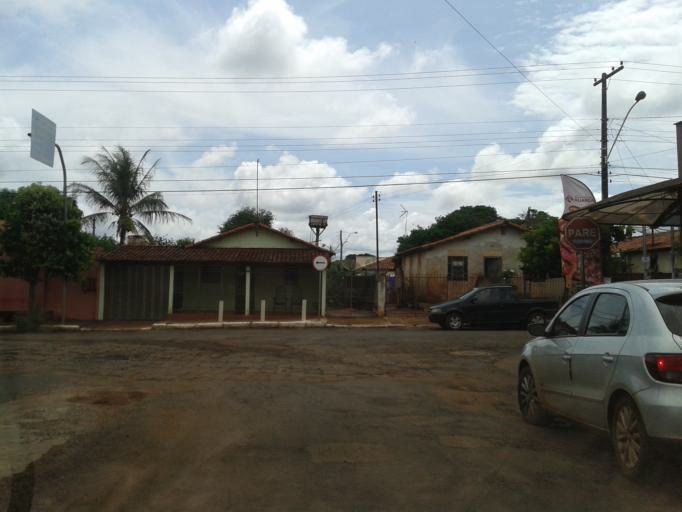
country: BR
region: Goias
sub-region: Buriti Alegre
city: Buriti Alegre
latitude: -18.1309
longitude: -49.0431
